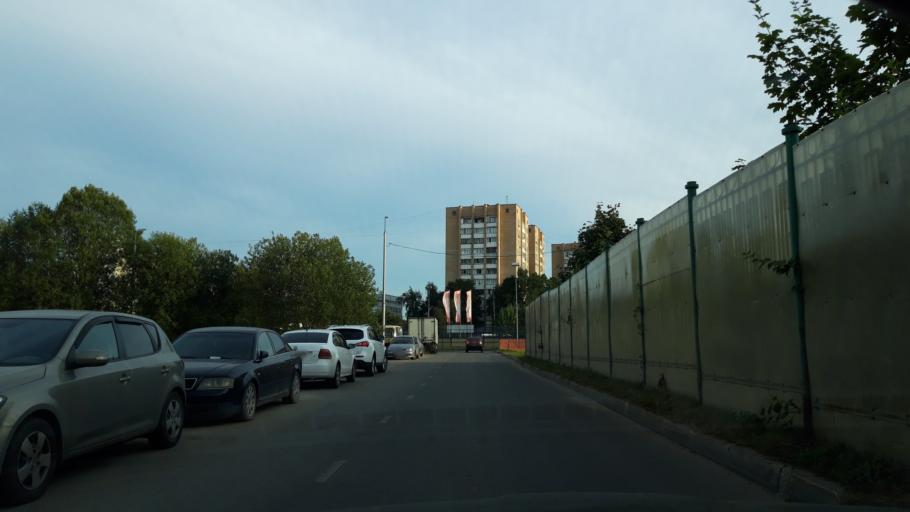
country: RU
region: Moscow
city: Zelenograd
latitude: 55.9811
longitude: 37.1891
